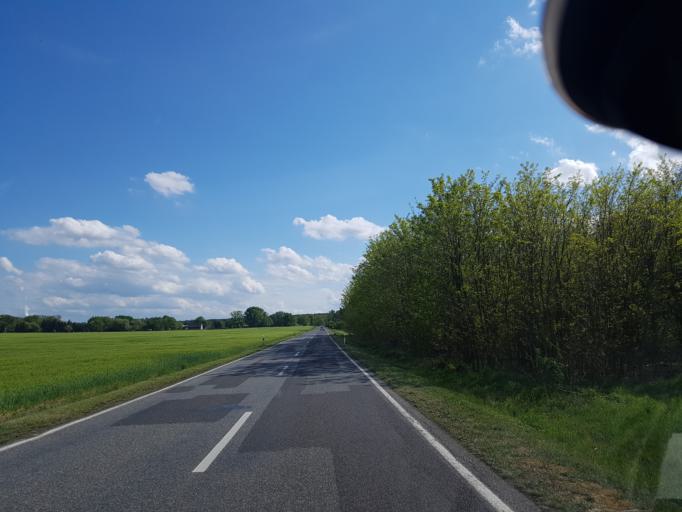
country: DE
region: Brandenburg
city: Drebkau
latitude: 51.6446
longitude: 14.2783
